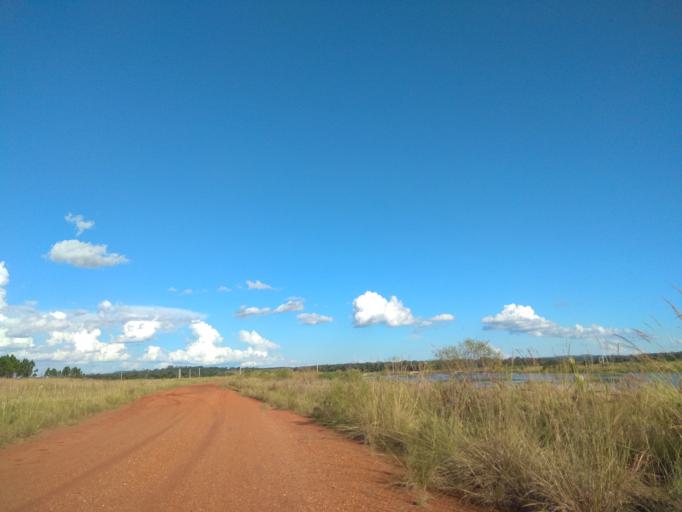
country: AR
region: Misiones
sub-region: Departamento de Candelaria
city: Candelaria
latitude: -27.4933
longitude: -55.7749
